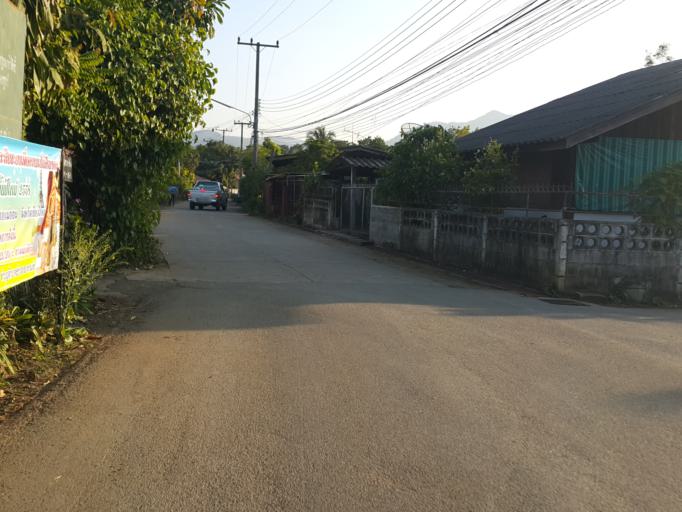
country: TH
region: Chiang Mai
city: Mae On
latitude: 18.7688
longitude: 99.2570
